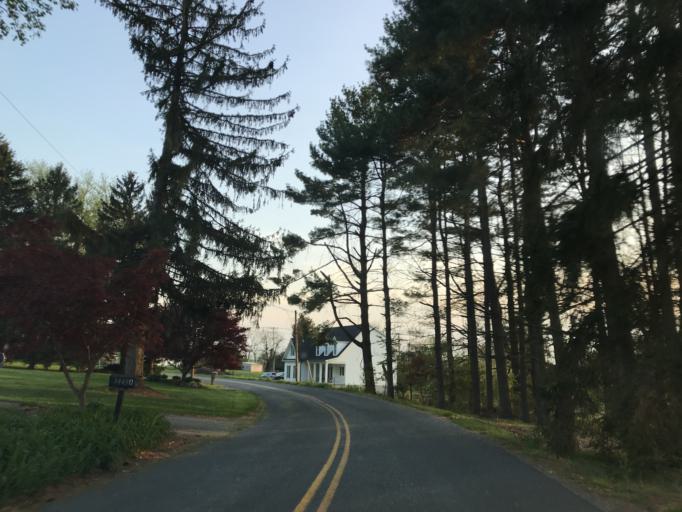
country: US
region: Maryland
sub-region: Harford County
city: Jarrettsville
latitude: 39.5904
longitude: -76.4296
